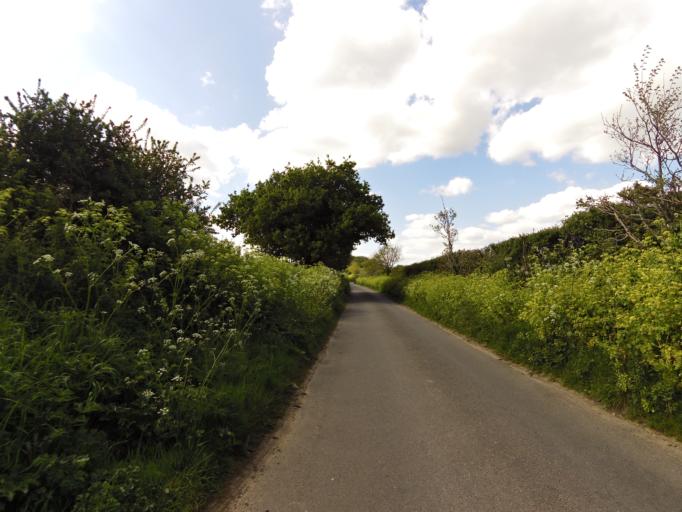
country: GB
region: England
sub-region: Suffolk
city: Kessingland
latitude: 52.4413
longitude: 1.6612
